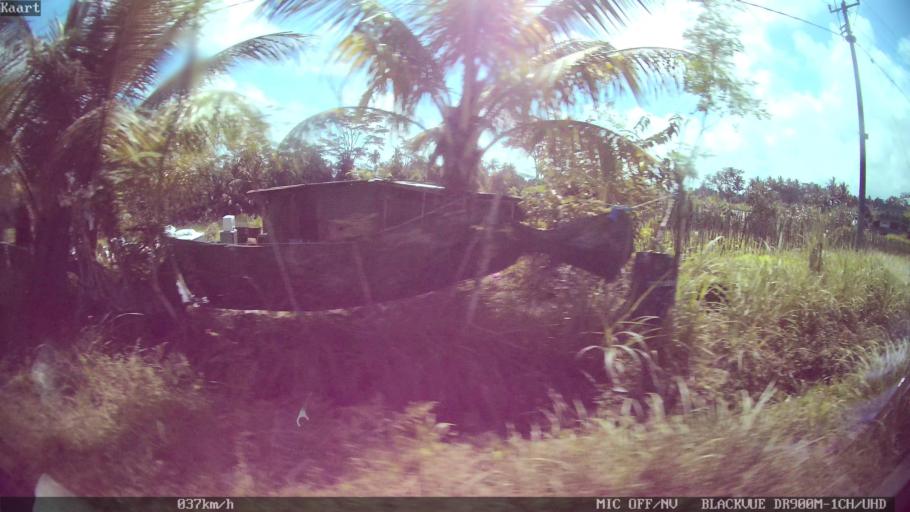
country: ID
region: Bali
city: Banjar Kelodan
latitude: -8.5092
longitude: 115.3368
